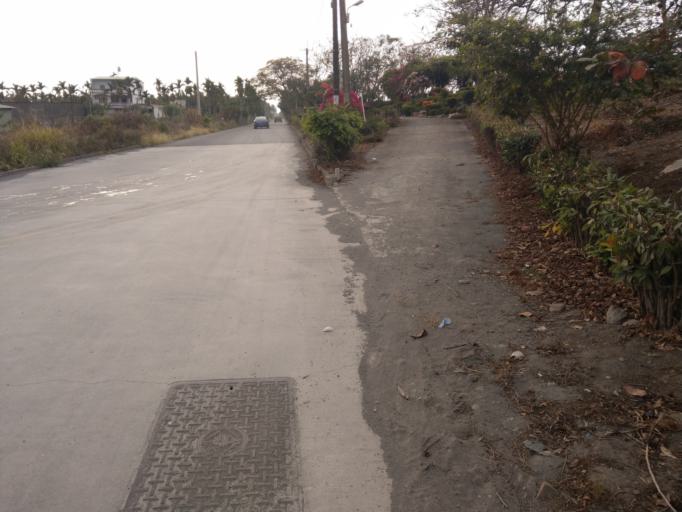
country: TW
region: Taiwan
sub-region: Pingtung
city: Pingtung
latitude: 22.7818
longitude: 120.5395
